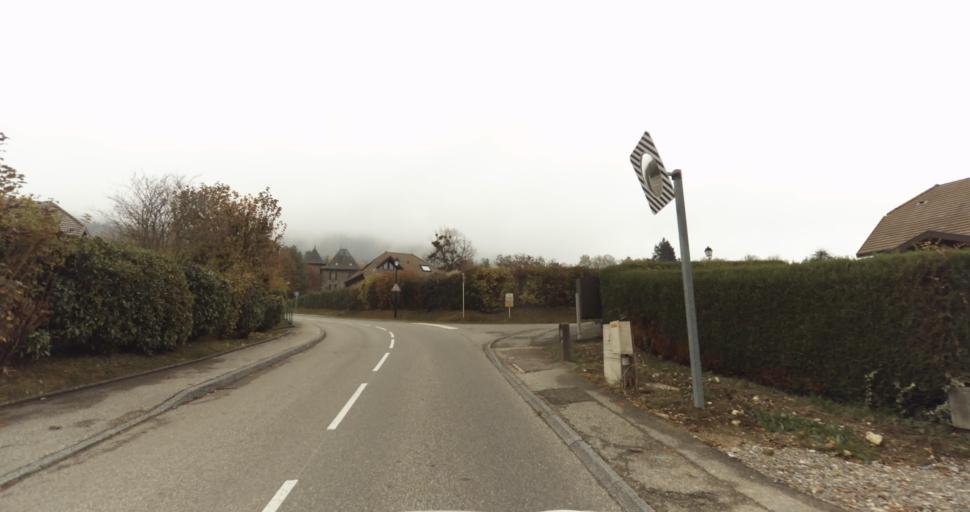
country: FR
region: Rhone-Alpes
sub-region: Departement de la Haute-Savoie
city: Viuz-la-Chiesaz
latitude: 45.8383
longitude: 6.0838
